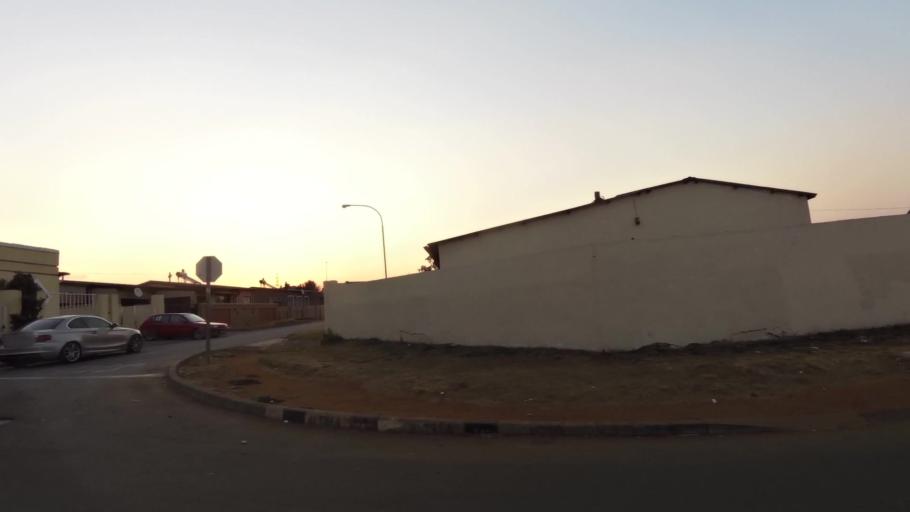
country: ZA
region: Gauteng
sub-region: City of Johannesburg Metropolitan Municipality
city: Soweto
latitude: -26.2845
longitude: 27.8801
